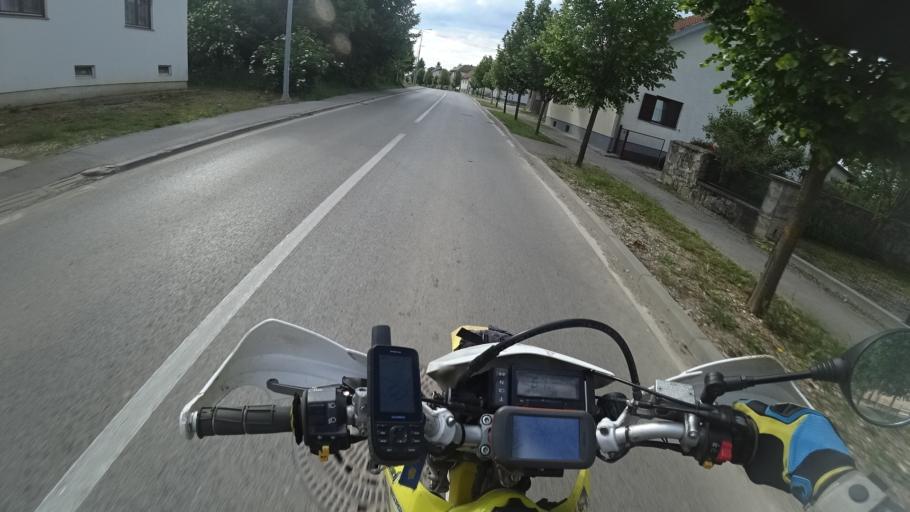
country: HR
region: Licko-Senjska
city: Gospic
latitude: 44.5398
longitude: 15.3839
